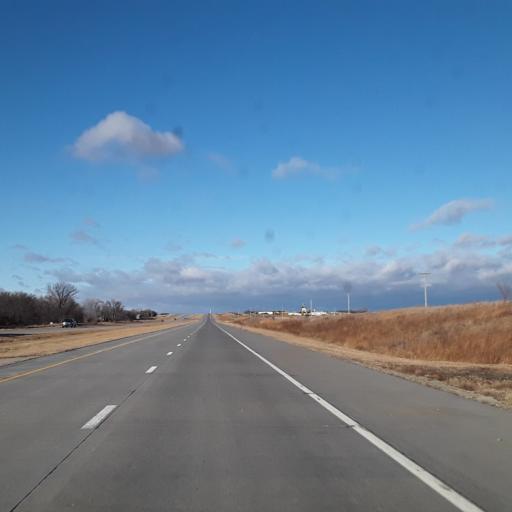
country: US
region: Kansas
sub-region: Republic County
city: Belleville
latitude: 39.8784
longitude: -97.6141
